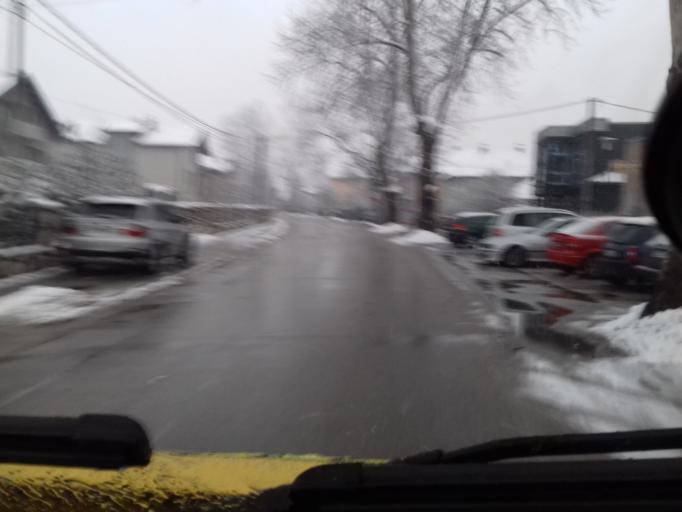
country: BA
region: Federation of Bosnia and Herzegovina
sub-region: Kanton Sarajevo
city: Sarajevo
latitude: 43.8234
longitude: 18.3220
